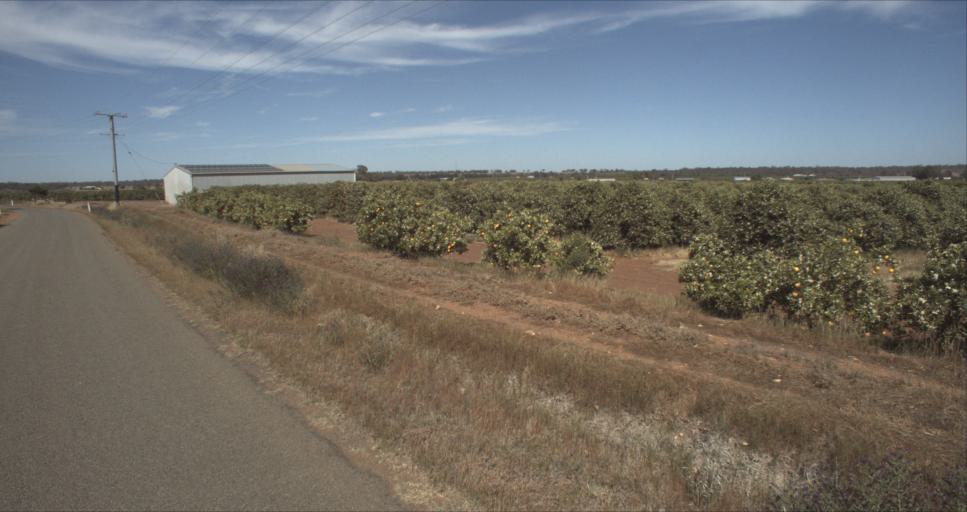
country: AU
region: New South Wales
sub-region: Leeton
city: Leeton
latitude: -34.5821
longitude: 146.4769
